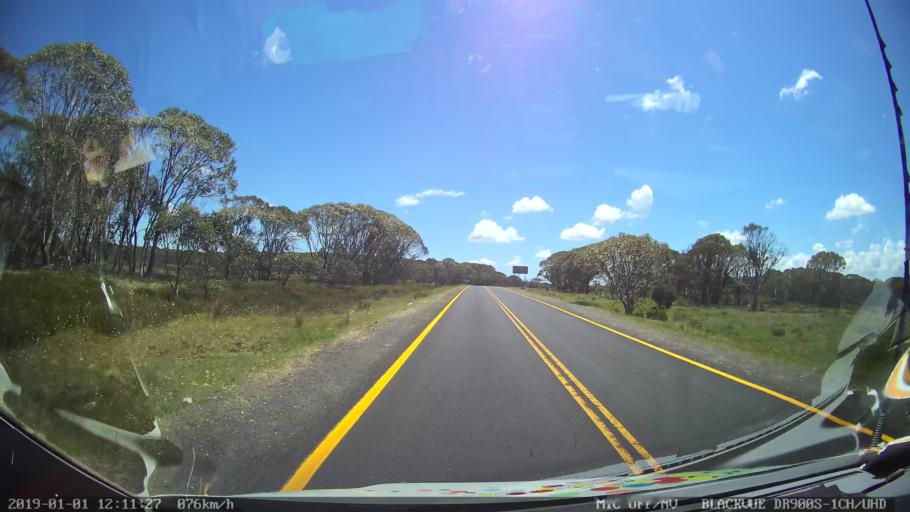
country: AU
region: New South Wales
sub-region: Tumut Shire
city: Tumut
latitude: -35.7839
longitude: 148.5081
